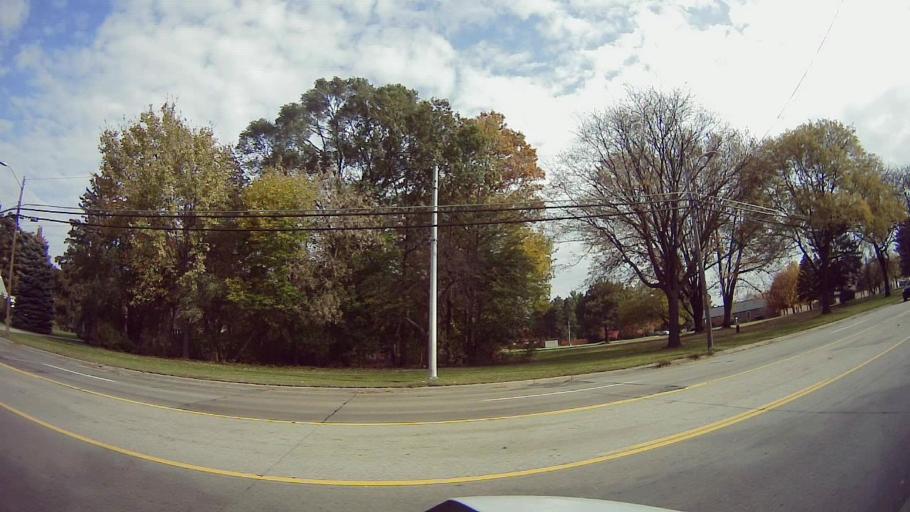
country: US
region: Michigan
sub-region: Oakland County
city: Madison Heights
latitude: 42.4999
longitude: -83.0674
